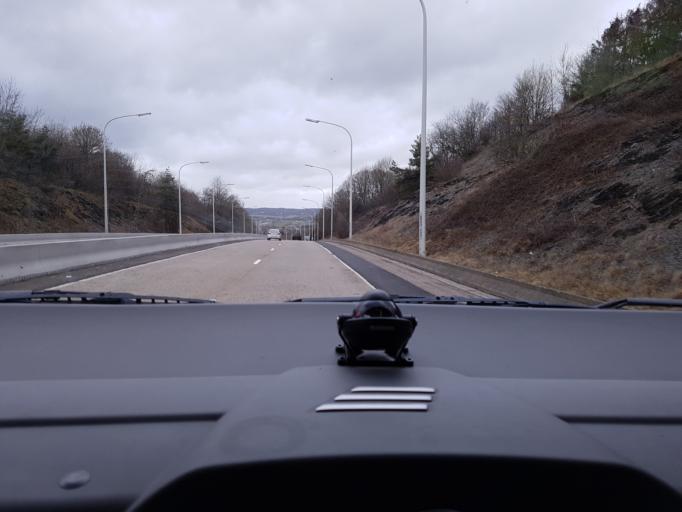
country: BE
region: Wallonia
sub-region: Province du Luxembourg
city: Marche-en-Famenne
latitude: 50.2590
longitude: 5.2638
